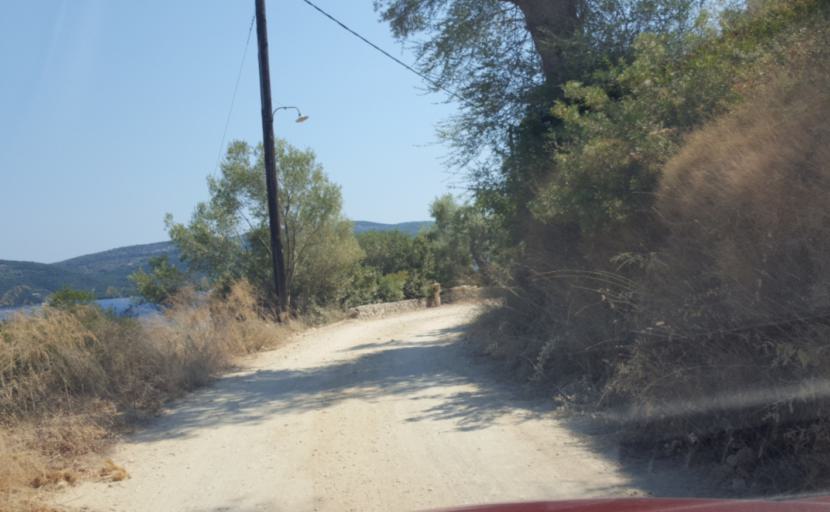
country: GR
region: Ionian Islands
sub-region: Lefkada
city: Nidri
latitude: 38.6694
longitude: 20.7117
